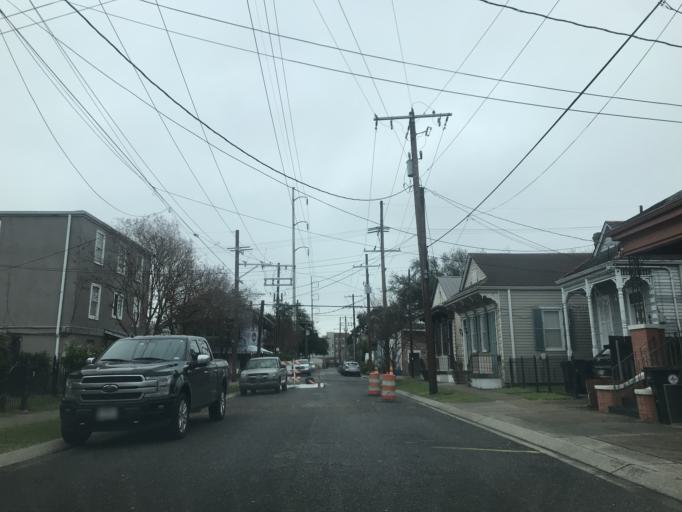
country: US
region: Louisiana
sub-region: Orleans Parish
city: New Orleans
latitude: 29.9725
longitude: -90.0963
